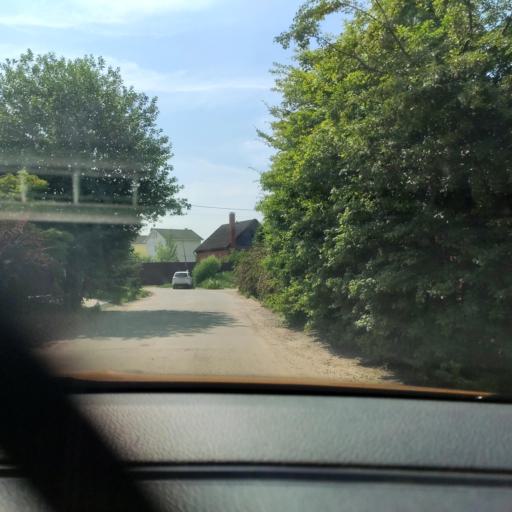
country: RU
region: Moscow
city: Severnyy
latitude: 55.9595
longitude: 37.5440
